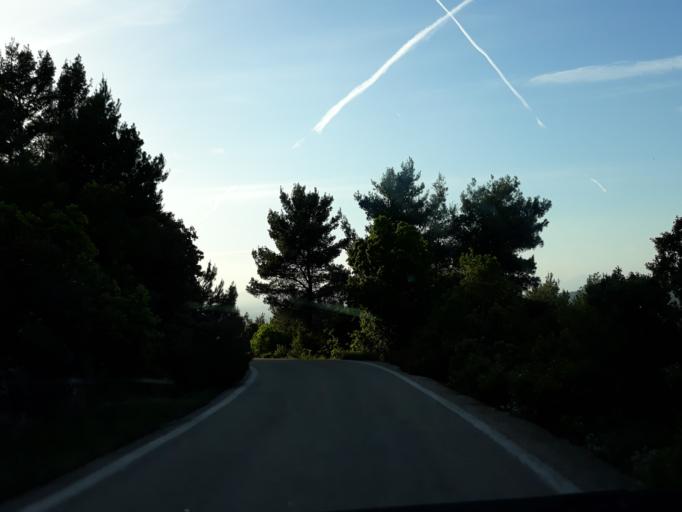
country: GR
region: Attica
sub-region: Nomarchia Anatolikis Attikis
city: Afidnes
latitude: 38.2273
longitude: 23.7950
